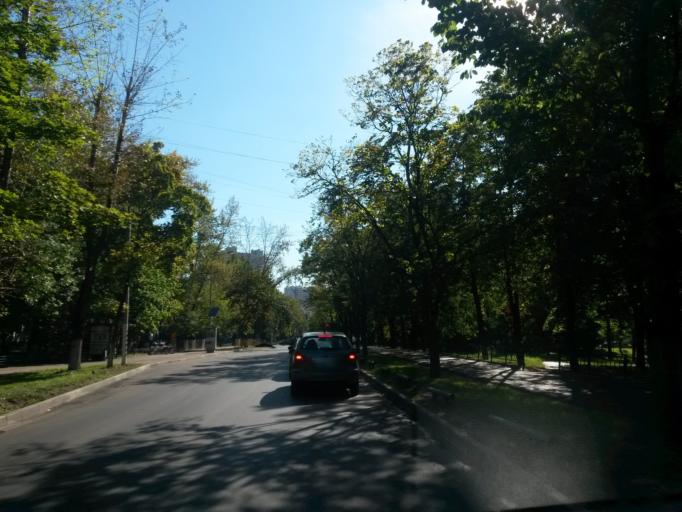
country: RU
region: Moscow
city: Kotlovka
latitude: 55.6596
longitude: 37.5946
